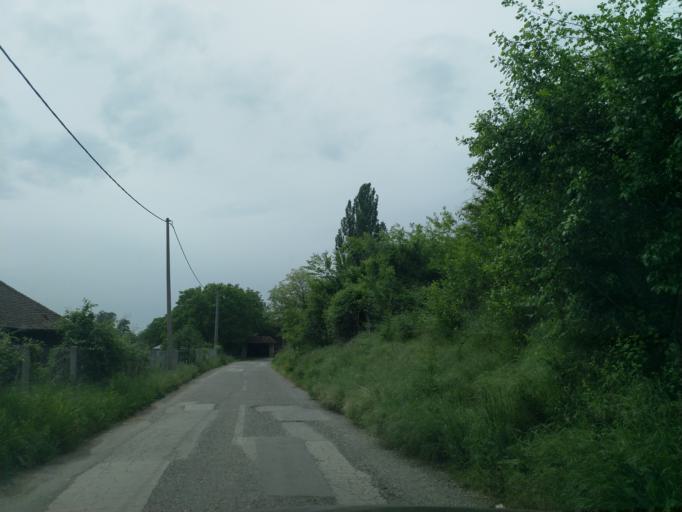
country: RS
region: Central Serbia
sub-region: Pomoravski Okrug
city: Paracin
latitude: 43.8636
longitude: 21.5845
